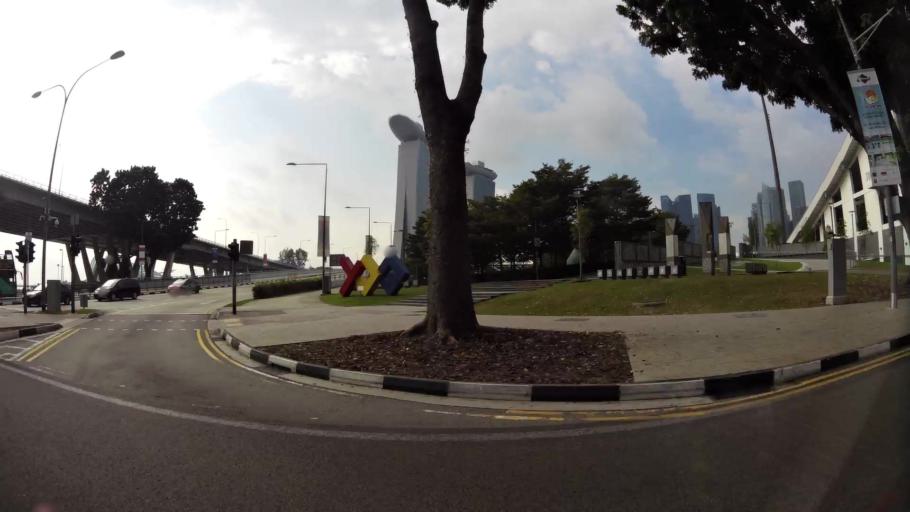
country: SG
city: Singapore
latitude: 1.2895
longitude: 103.8606
